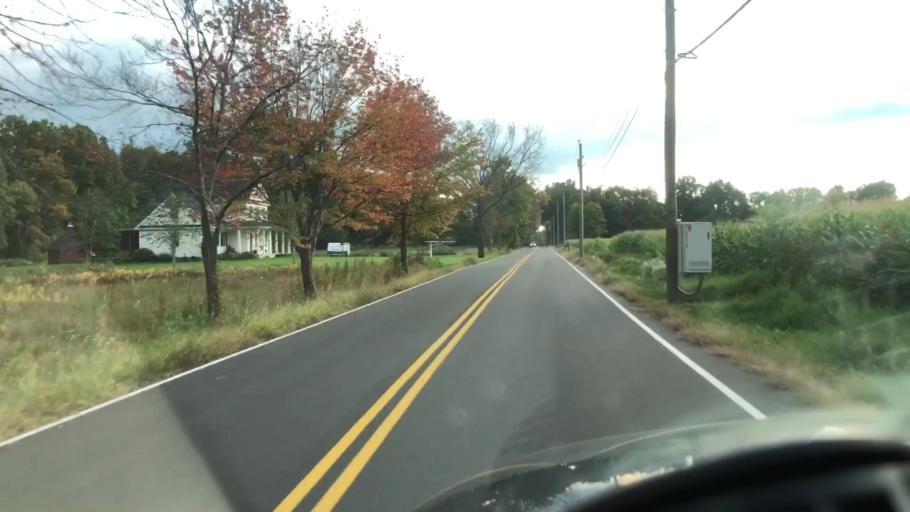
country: US
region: Connecticut
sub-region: Hartford County
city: Suffield Depot
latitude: 42.0157
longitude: -72.6558
